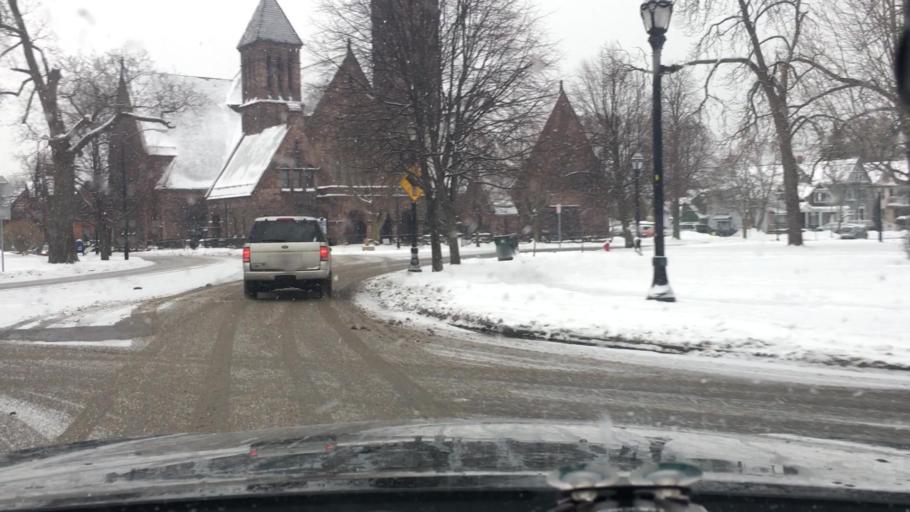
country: US
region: New York
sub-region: Erie County
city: Buffalo
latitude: 42.9024
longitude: -78.8820
